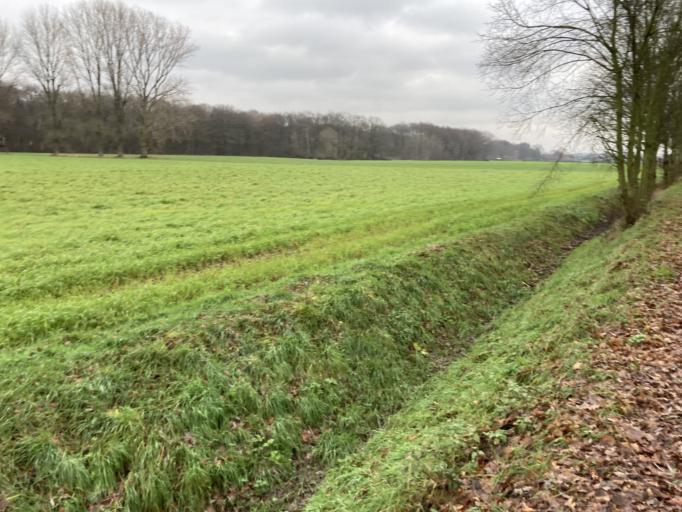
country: DE
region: North Rhine-Westphalia
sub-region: Regierungsbezirk Dusseldorf
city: Meerbusch
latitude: 51.2828
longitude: 6.6249
